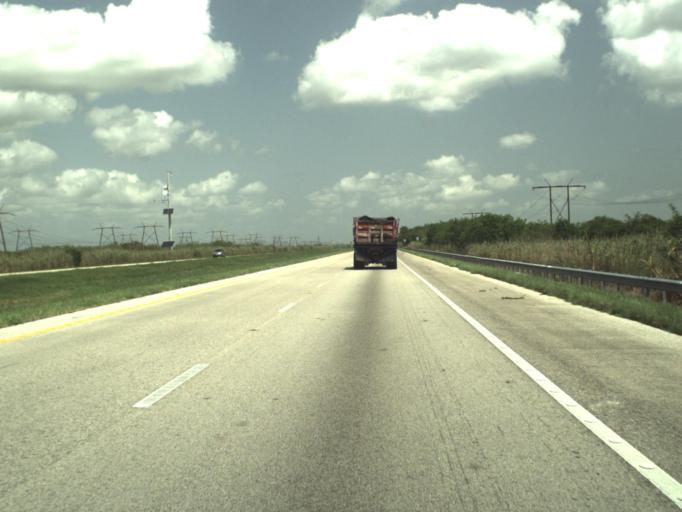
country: US
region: Florida
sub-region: Broward County
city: Weston
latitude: 26.2783
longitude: -80.4940
